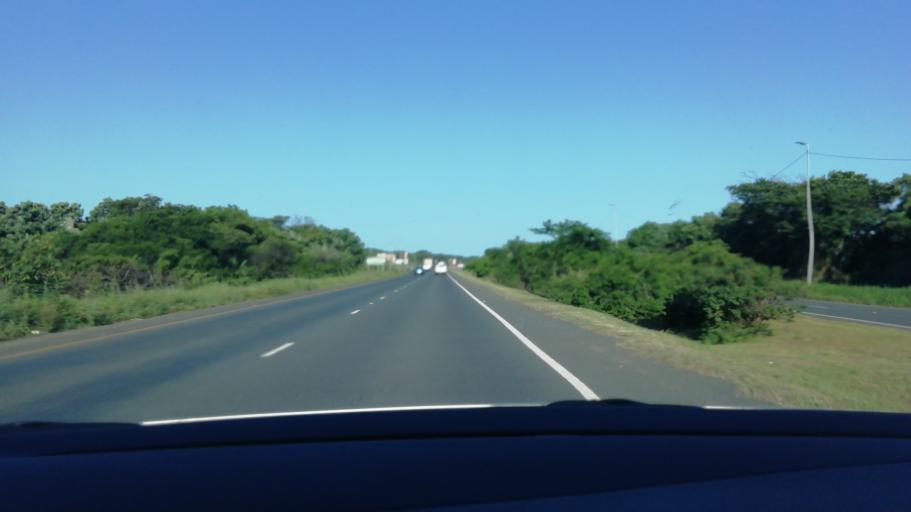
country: ZA
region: KwaZulu-Natal
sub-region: uThungulu District Municipality
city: Richards Bay
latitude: -28.7686
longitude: 32.0459
